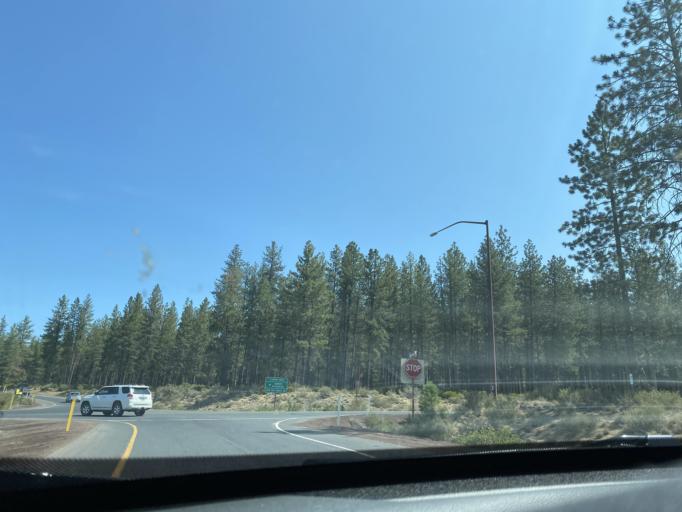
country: US
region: Oregon
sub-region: Deschutes County
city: Sunriver
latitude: 43.8688
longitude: -121.4018
